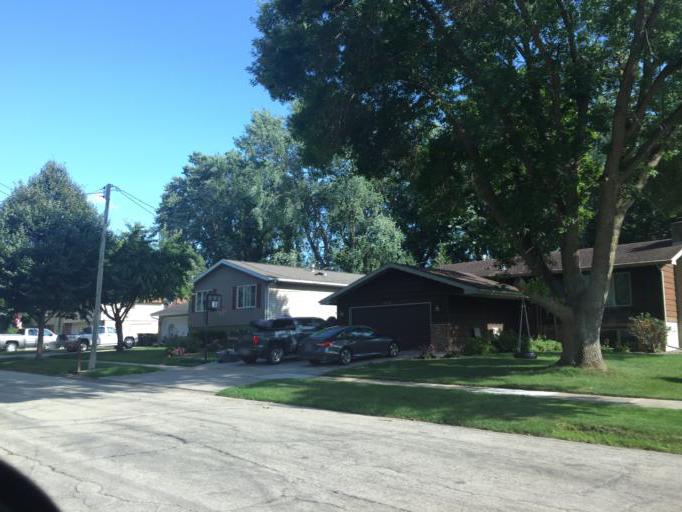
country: US
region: Minnesota
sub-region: Olmsted County
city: Rochester
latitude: 44.0448
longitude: -92.4975
